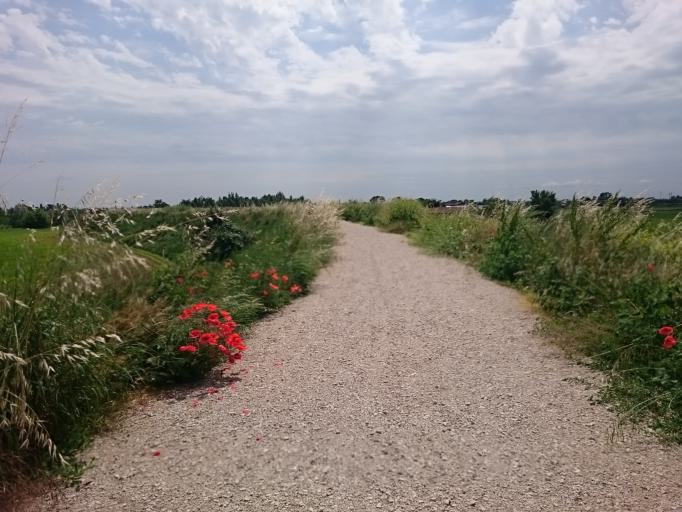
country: IT
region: Veneto
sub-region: Provincia di Padova
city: Carceri
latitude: 45.2014
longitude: 11.6460
